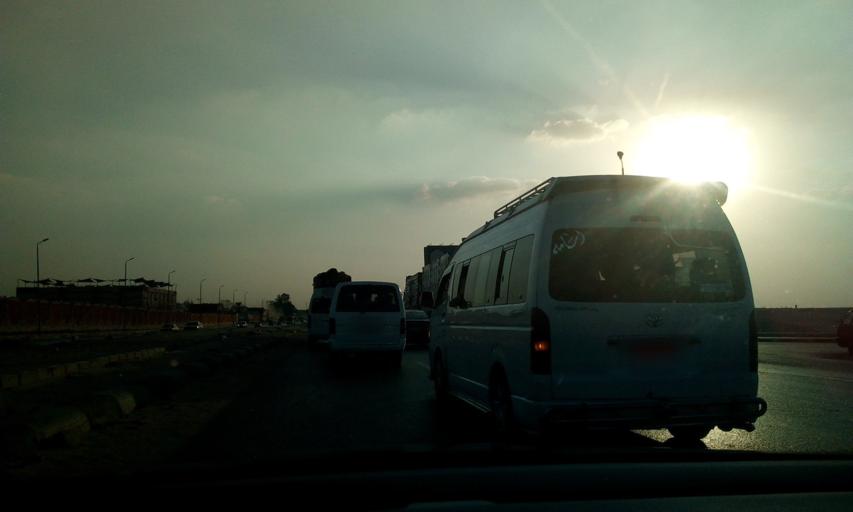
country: EG
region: Muhafazat al Qalyubiyah
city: Al Khankah
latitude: 30.1537
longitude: 31.4416
